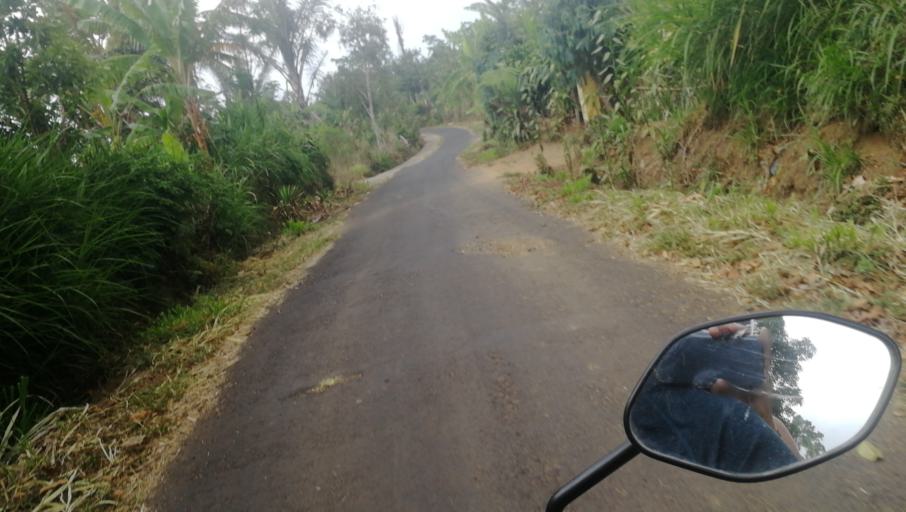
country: ID
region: Bali
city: Banjar Ambengan
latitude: -8.2206
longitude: 115.1100
